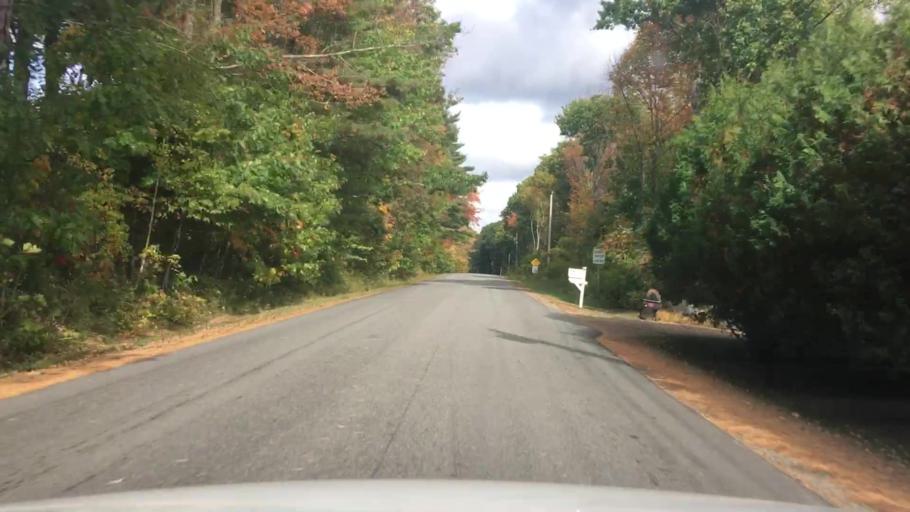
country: US
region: Maine
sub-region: Knox County
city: Camden
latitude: 44.2186
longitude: -69.1014
